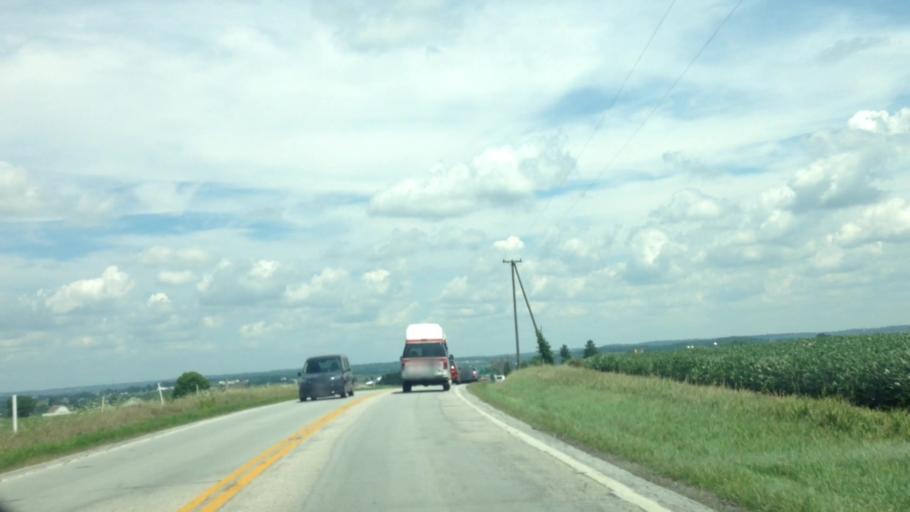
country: US
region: Ohio
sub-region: Wayne County
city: Rittman
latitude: 40.9103
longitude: -81.7967
